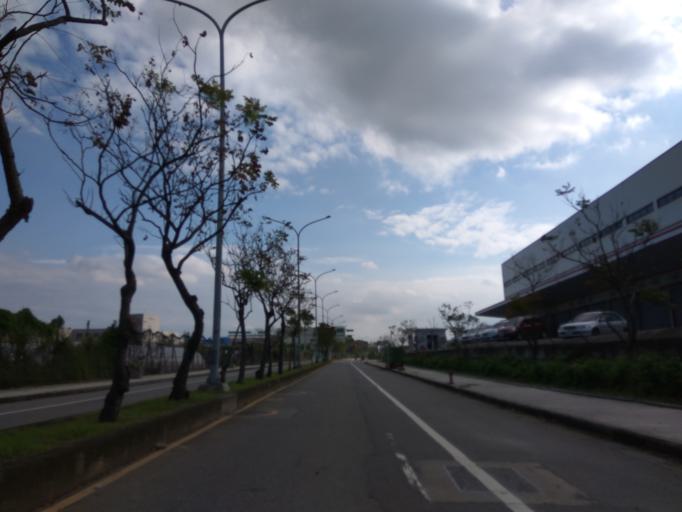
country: TW
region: Taiwan
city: Taoyuan City
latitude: 25.0604
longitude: 121.1786
